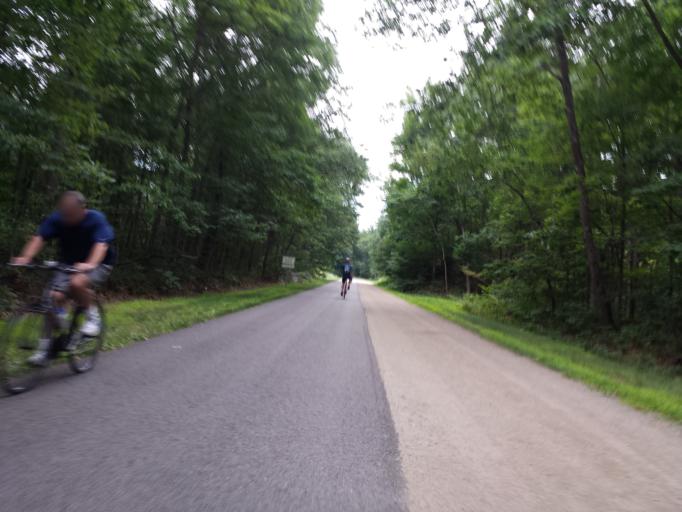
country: US
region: New York
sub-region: Dutchess County
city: Hillside Lake
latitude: 41.5965
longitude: -73.8323
